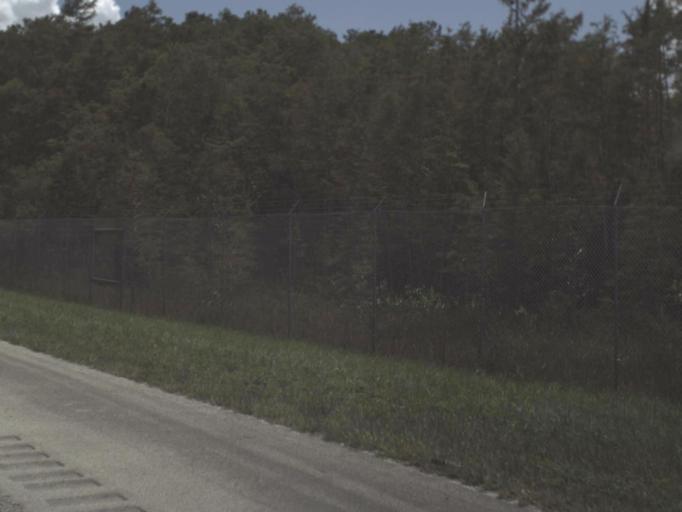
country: US
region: Florida
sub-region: Collier County
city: Immokalee
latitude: 26.1677
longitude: -81.1289
